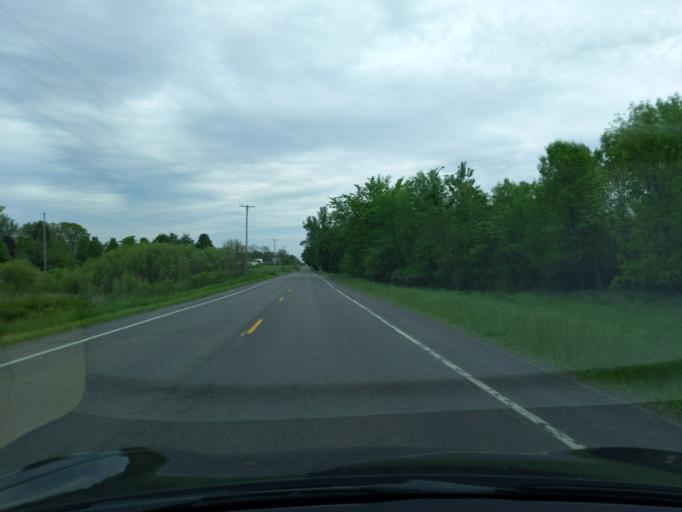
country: US
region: Michigan
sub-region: Ingham County
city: Mason
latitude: 42.5600
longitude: -84.3568
